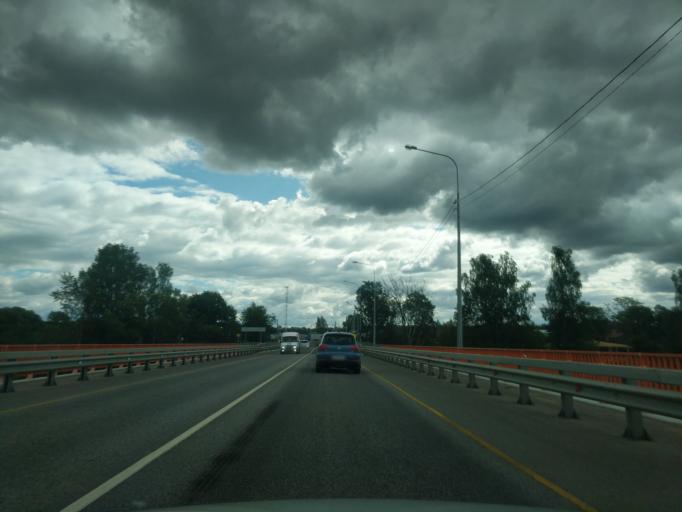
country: RU
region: Jaroslavl
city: Tunoshna
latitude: 57.5428
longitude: 40.1168
